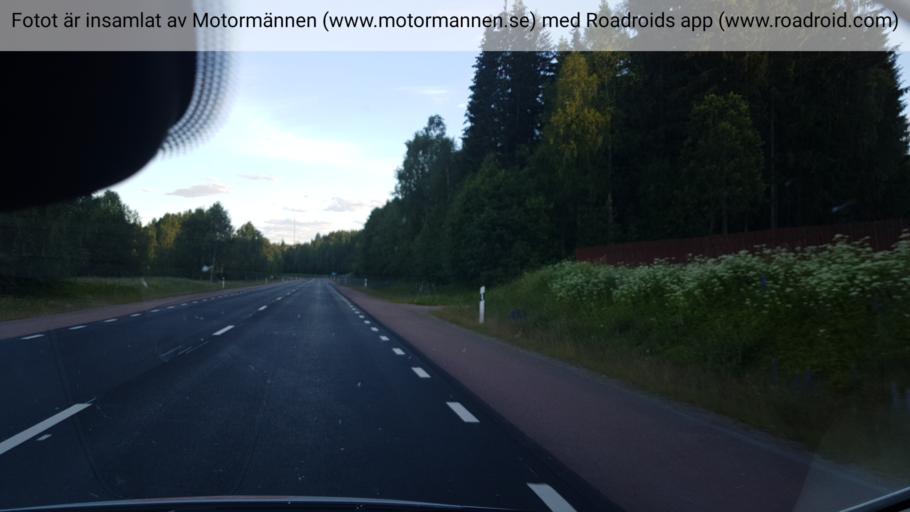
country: SE
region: Vaermland
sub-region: Torsby Kommun
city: Torsby
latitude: 60.2089
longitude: 13.0156
